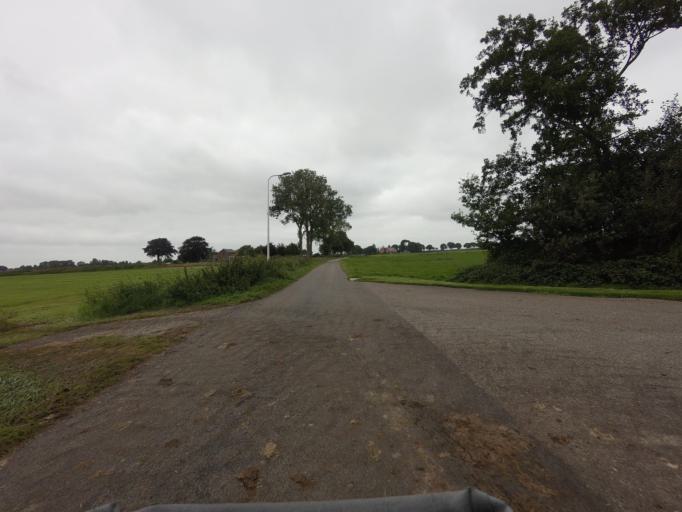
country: NL
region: Overijssel
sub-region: Gemeente Steenwijkerland
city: Blokzijl
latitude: 52.7400
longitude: 6.0062
